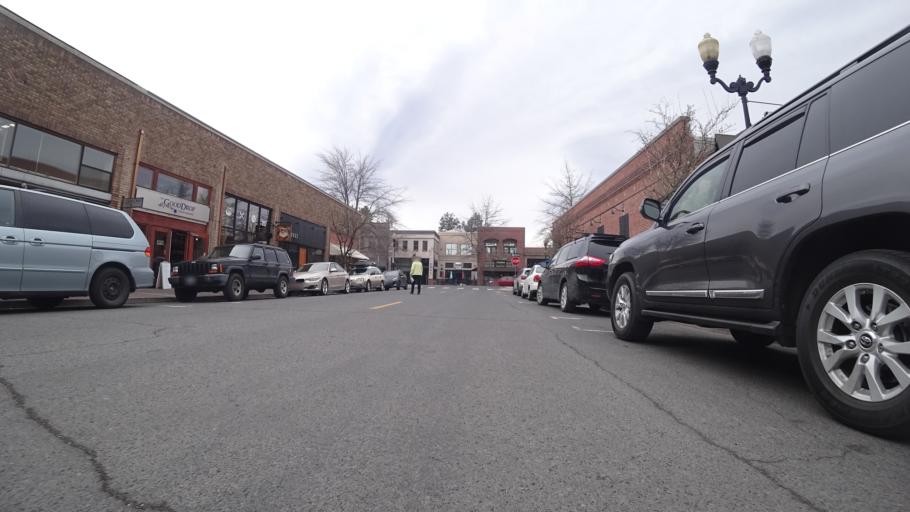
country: US
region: Oregon
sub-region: Deschutes County
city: Bend
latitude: 44.0586
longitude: -121.3138
